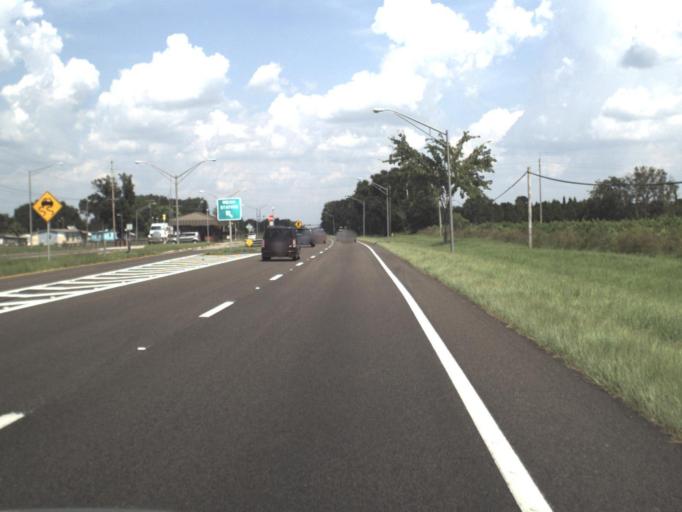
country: US
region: Florida
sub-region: Hillsborough County
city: Plant City
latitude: 27.9375
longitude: -82.1153
